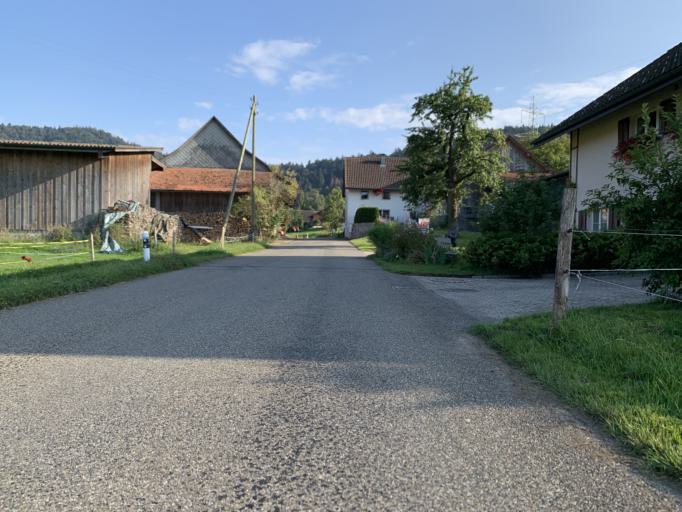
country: CH
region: Zurich
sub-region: Bezirk Hinwil
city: Baretswil
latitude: 47.3234
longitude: 8.8695
